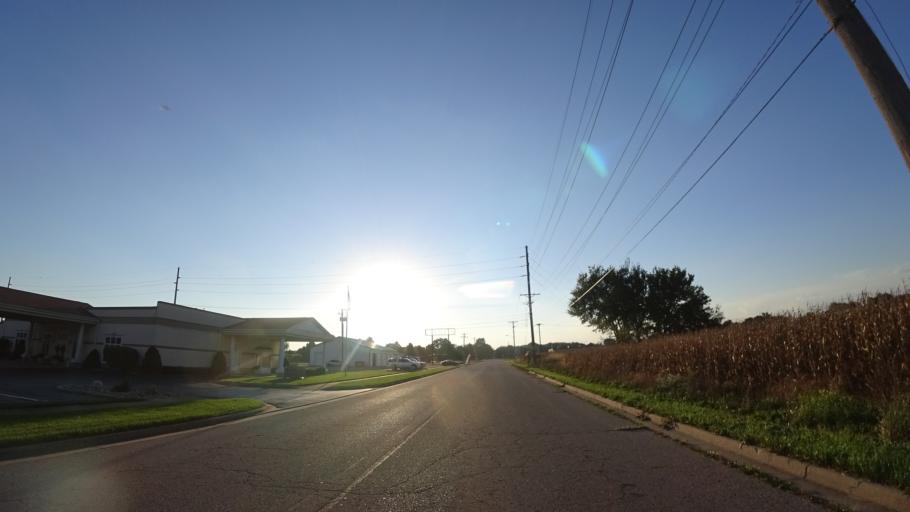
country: US
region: Michigan
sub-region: Saint Joseph County
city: Three Rivers
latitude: 41.9492
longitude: -85.6448
